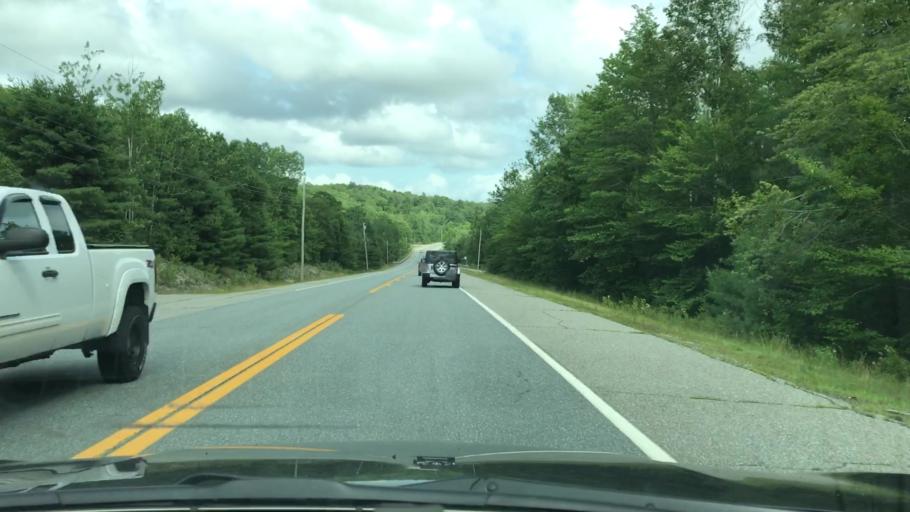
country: US
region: Maine
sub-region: Hancock County
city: Surry
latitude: 44.5641
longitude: -68.5977
